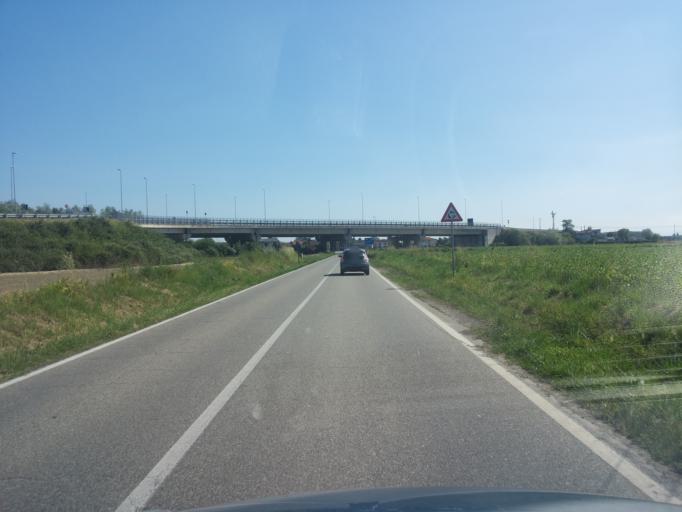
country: IT
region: Piedmont
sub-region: Provincia di Vercelli
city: Borgo Vercelli
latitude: 45.3658
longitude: 8.4611
